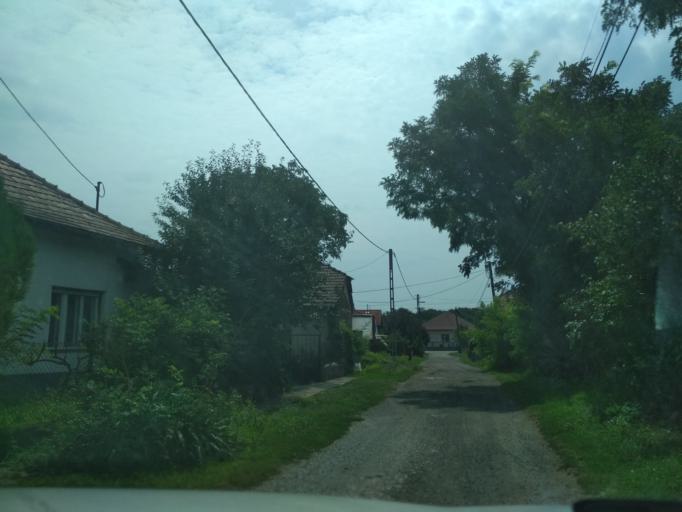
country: HU
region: Jasz-Nagykun-Szolnok
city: Tiszafured
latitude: 47.6110
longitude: 20.7625
